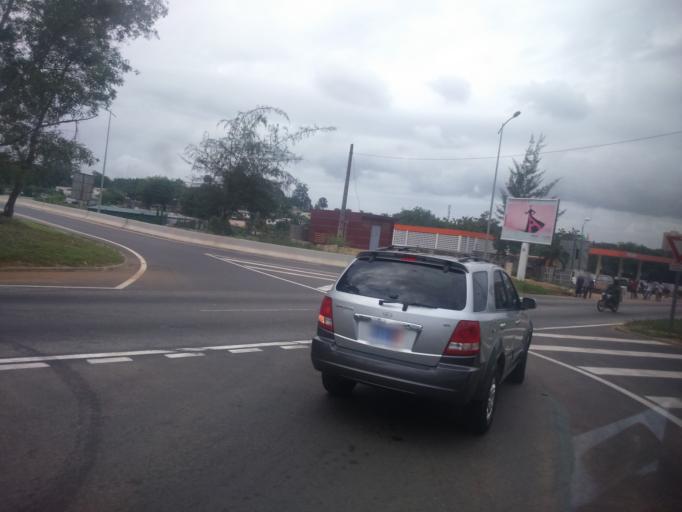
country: CI
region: Lagunes
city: Abidjan
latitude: 5.3534
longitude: -4.0019
